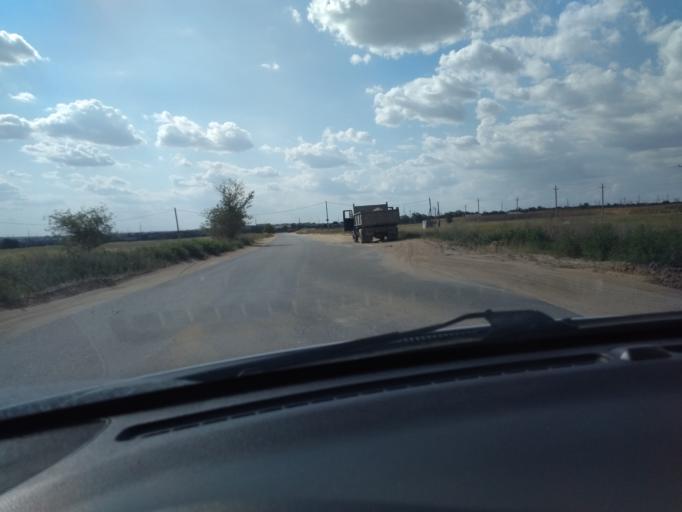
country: RU
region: Volgograd
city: Vodstroy
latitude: 48.8055
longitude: 44.5285
